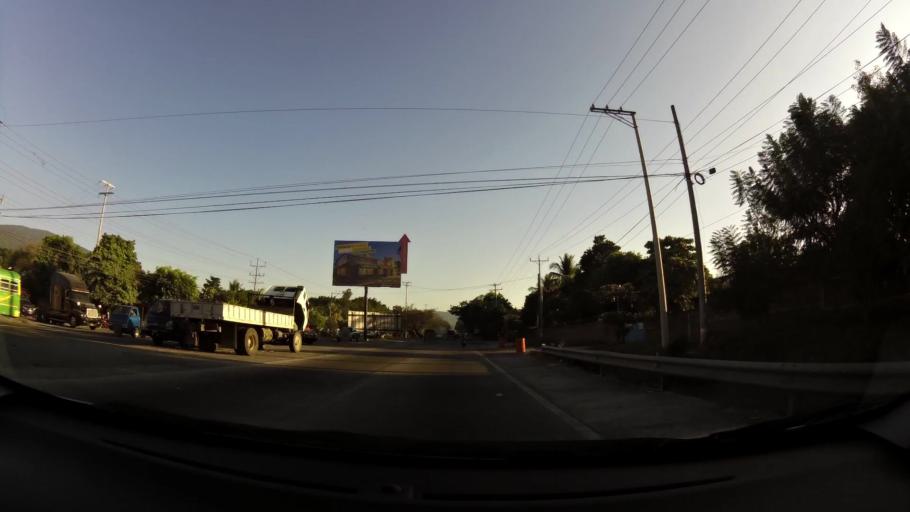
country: SV
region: La Libertad
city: Ciudad Arce
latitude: 13.7600
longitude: -89.3681
